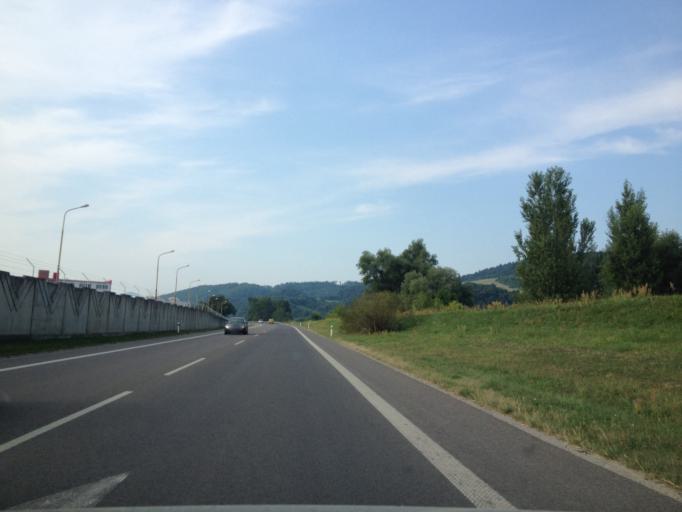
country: SK
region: Nitriansky
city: Puchov
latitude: 49.1078
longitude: 18.3136
